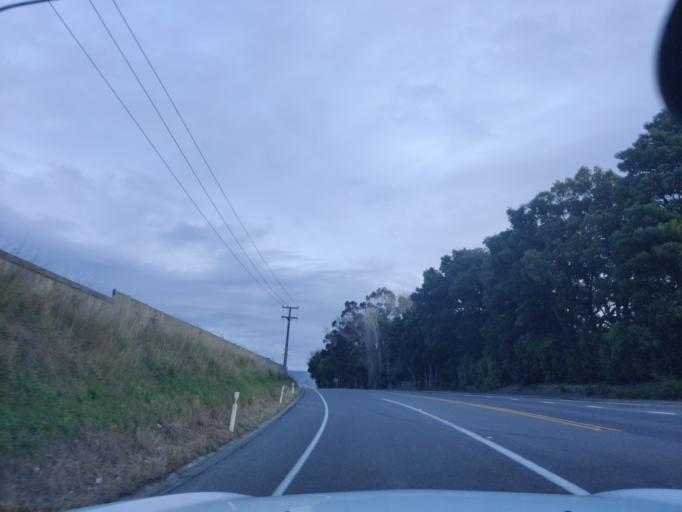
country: NZ
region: Manawatu-Wanganui
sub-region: Palmerston North City
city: Palmerston North
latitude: -40.3815
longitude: 175.6470
